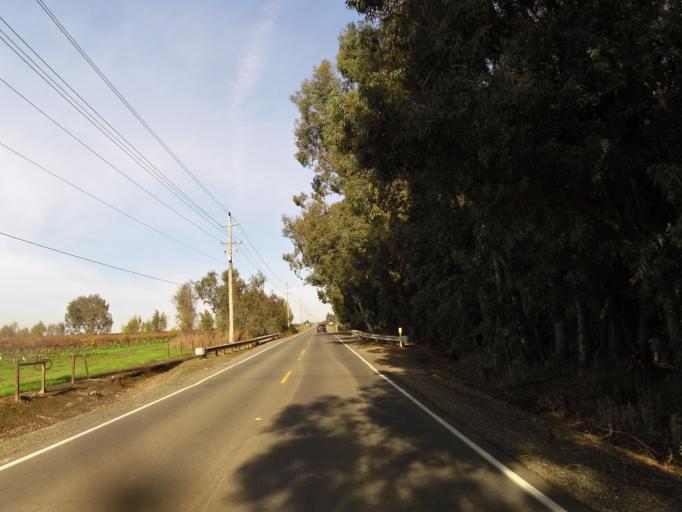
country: US
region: California
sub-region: Sacramento County
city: Laguna
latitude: 38.3578
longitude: -121.4175
